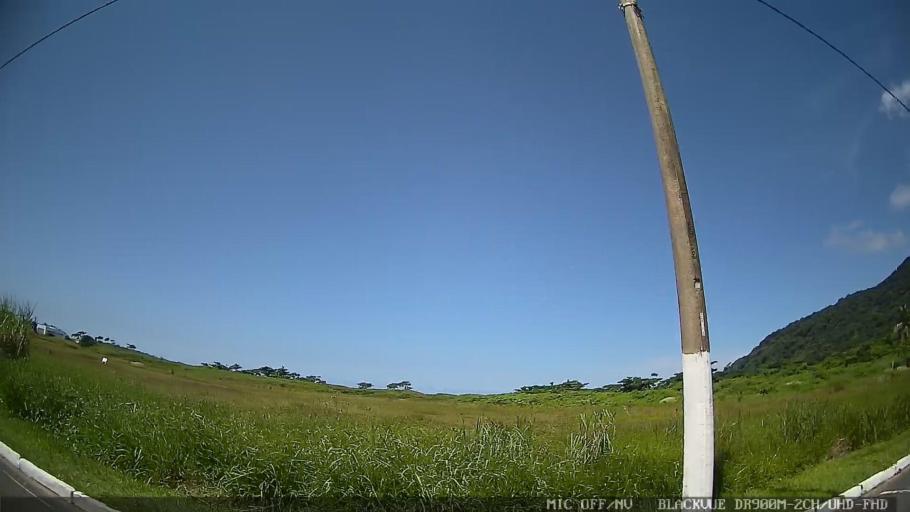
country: BR
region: Sao Paulo
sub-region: Peruibe
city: Peruibe
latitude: -24.3297
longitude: -47.0018
